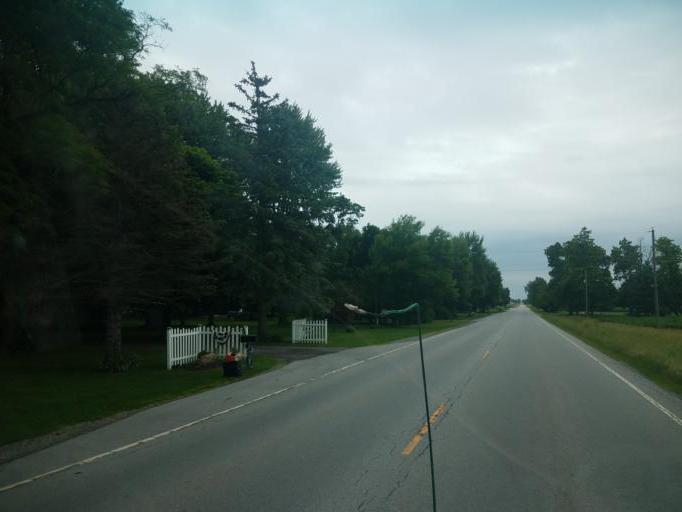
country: US
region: Ohio
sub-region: Hardin County
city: Ada
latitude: 40.7440
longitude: -83.8232
